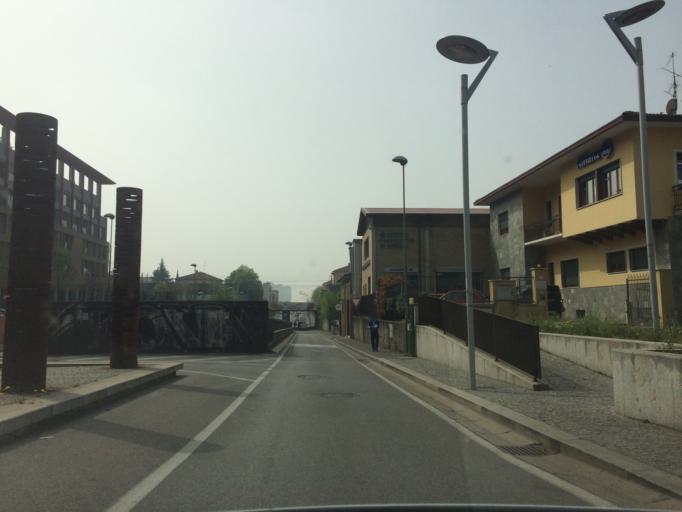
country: IT
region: Lombardy
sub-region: Provincia di Brescia
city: Brescia
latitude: 45.5353
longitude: 10.2017
